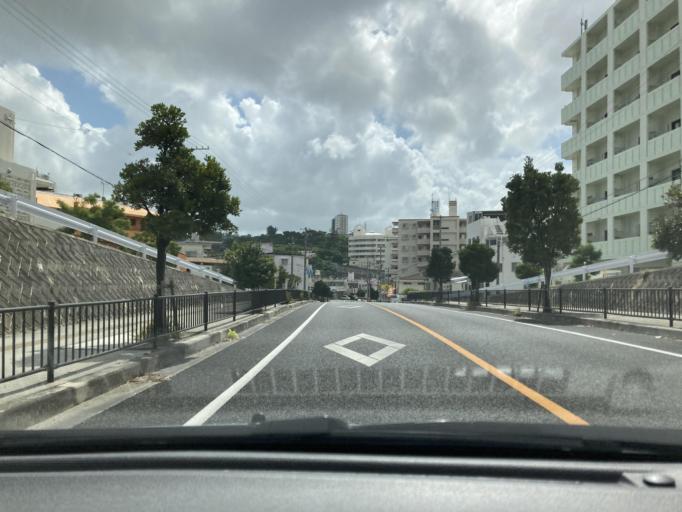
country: JP
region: Okinawa
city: Ginowan
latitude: 26.2630
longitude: 127.7298
